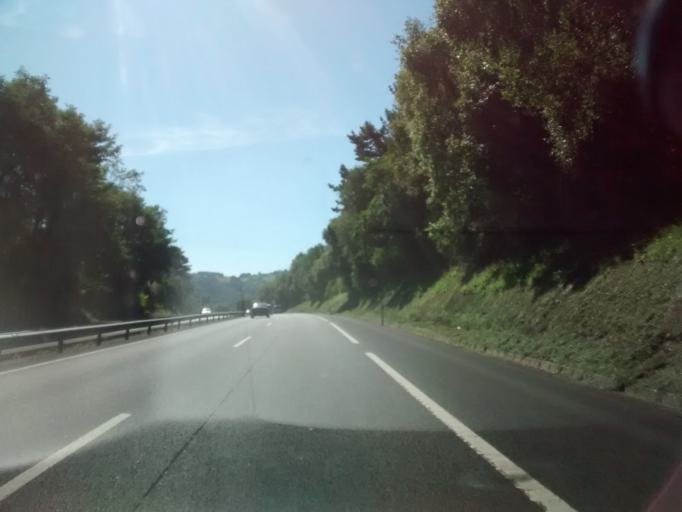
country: ES
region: Basque Country
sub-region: Provincia de Guipuzcoa
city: Zarautz
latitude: 43.2808
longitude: -2.1777
